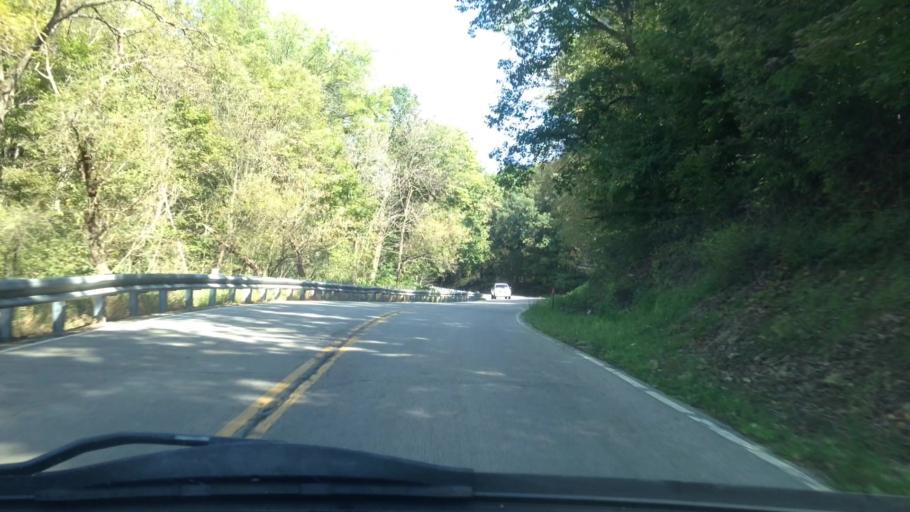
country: US
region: Minnesota
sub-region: Fillmore County
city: Rushford
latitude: 43.6867
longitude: -91.7809
